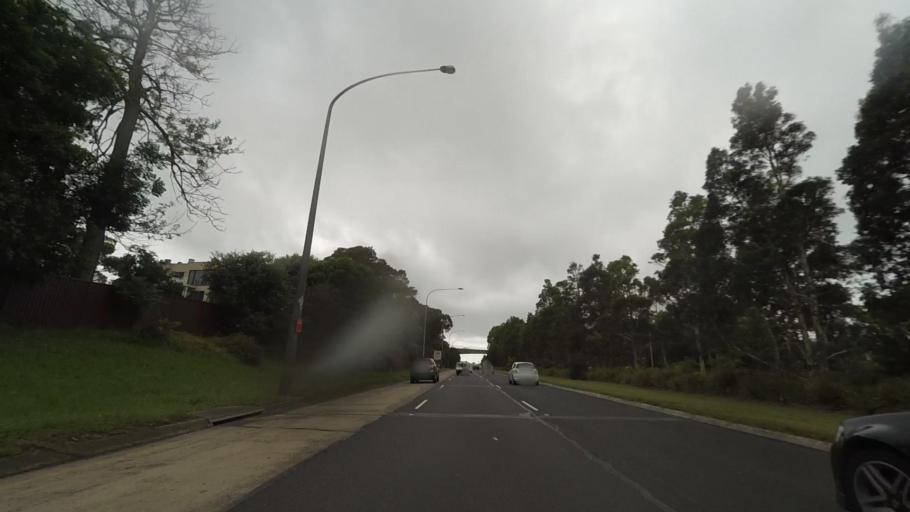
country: AU
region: New South Wales
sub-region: Kogarah
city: Blakehurst
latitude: -34.0145
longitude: 151.1240
